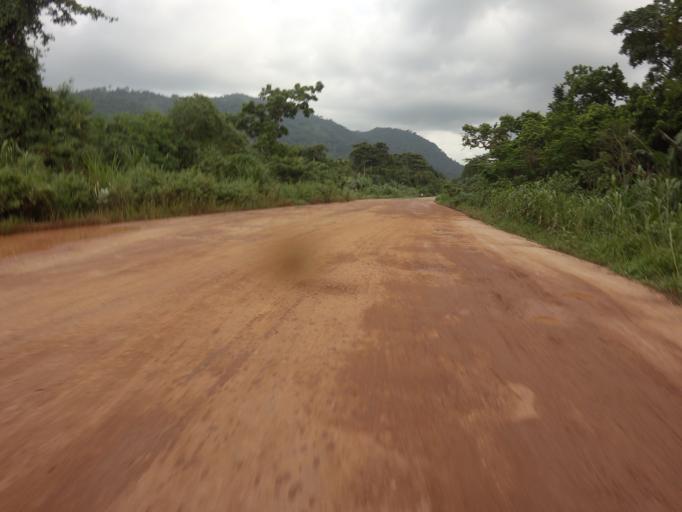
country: GH
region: Volta
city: Kpandu
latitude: 6.8109
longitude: 0.3751
